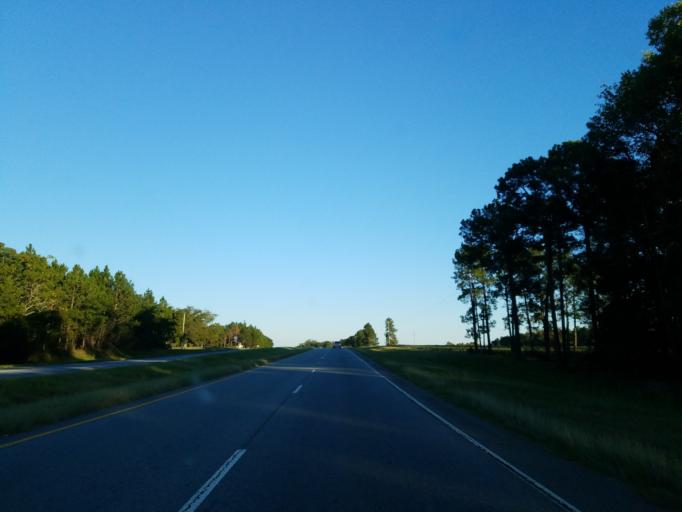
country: US
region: Georgia
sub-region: Worth County
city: Sylvester
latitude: 31.4841
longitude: -83.6958
